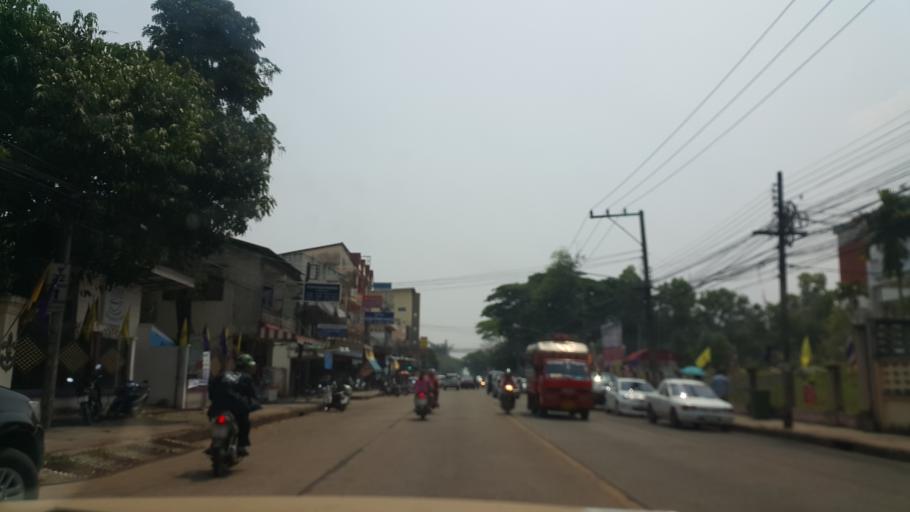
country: TH
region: Nakhon Phanom
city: Nakhon Phanom
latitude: 17.4115
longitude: 104.7793
